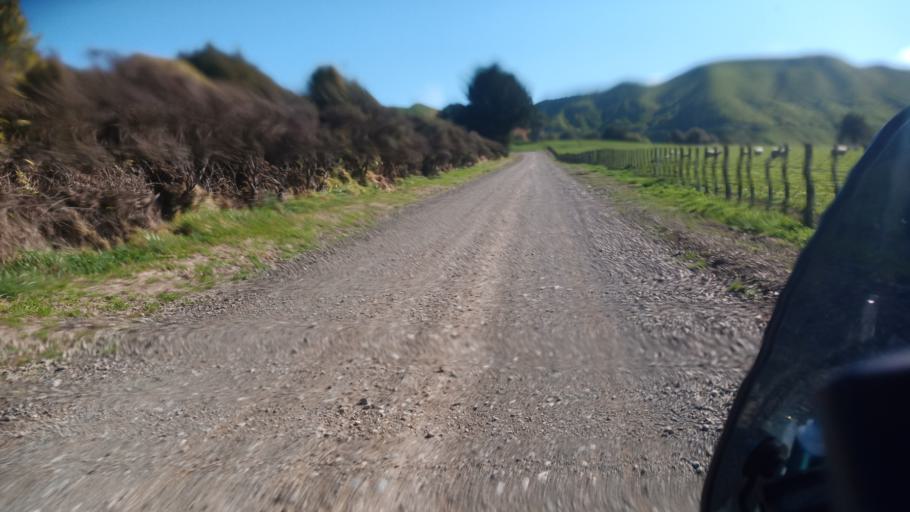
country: NZ
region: Gisborne
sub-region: Gisborne District
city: Gisborne
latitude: -39.1544
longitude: 177.9152
